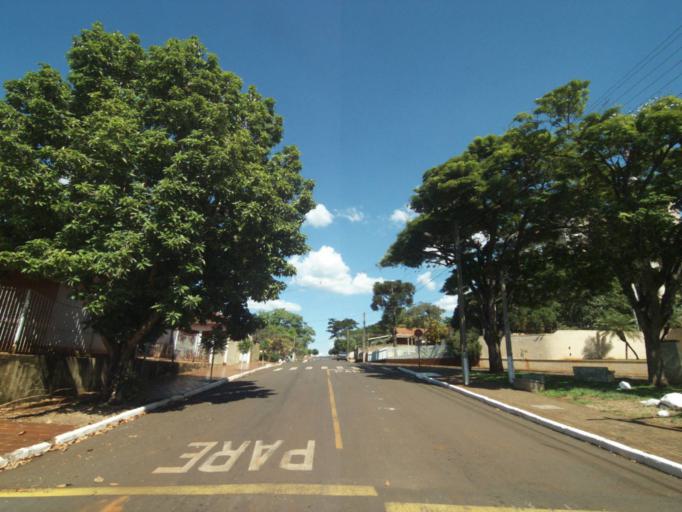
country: BR
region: Parana
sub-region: Sertanopolis
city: Sertanopolis
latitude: -23.0412
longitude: -50.8160
